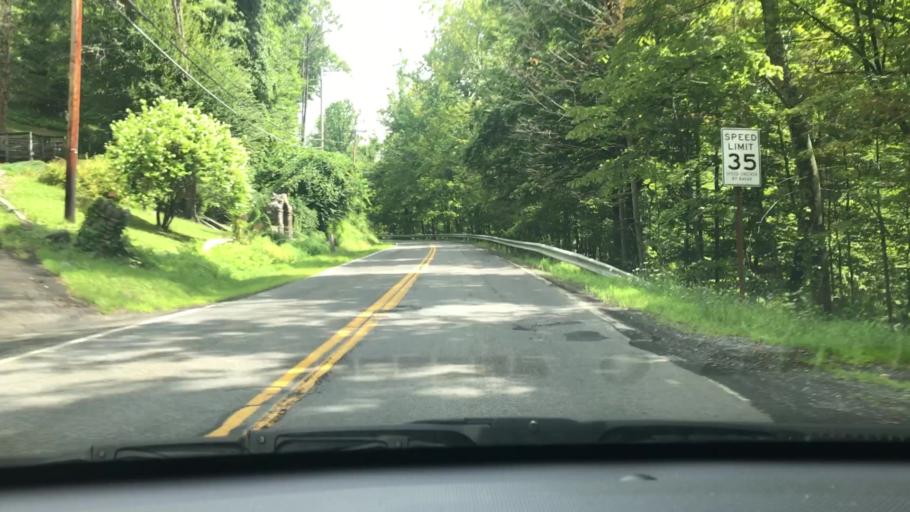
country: US
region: New York
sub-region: Ulster County
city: Shokan
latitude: 41.9793
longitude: -74.2773
